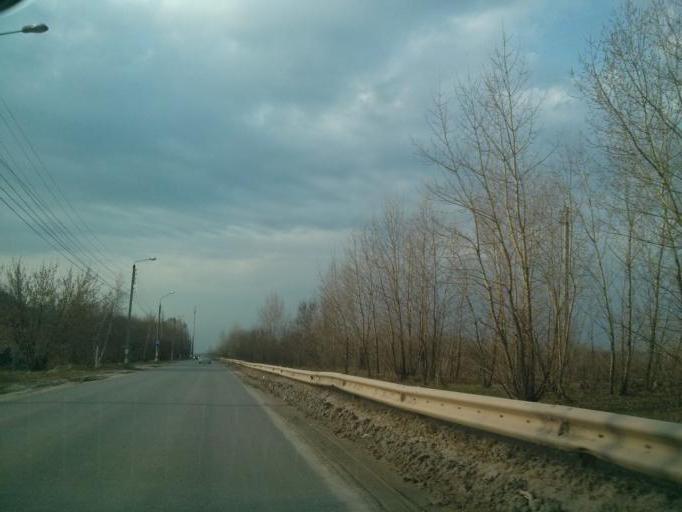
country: RU
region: Nizjnij Novgorod
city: Afonino
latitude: 56.3017
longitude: 44.1016
